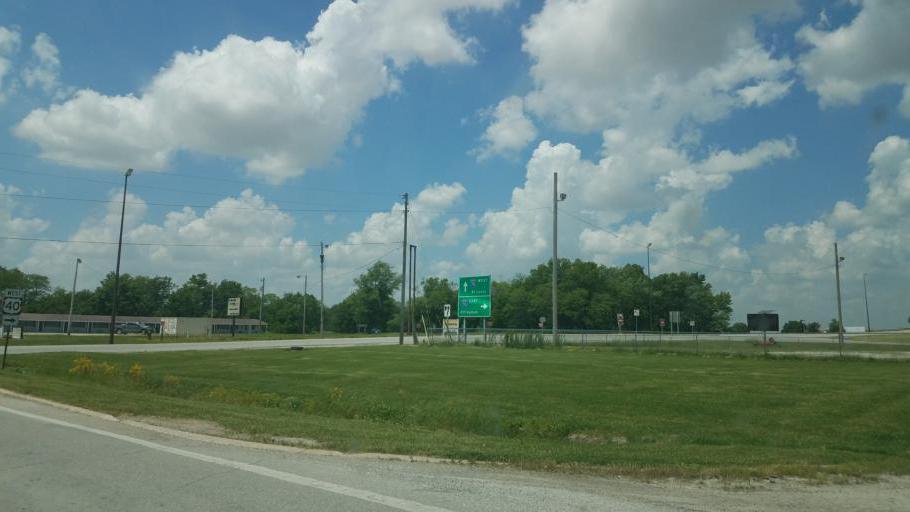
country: US
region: Illinois
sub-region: Bond County
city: Greenville
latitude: 38.8289
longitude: -89.5449
